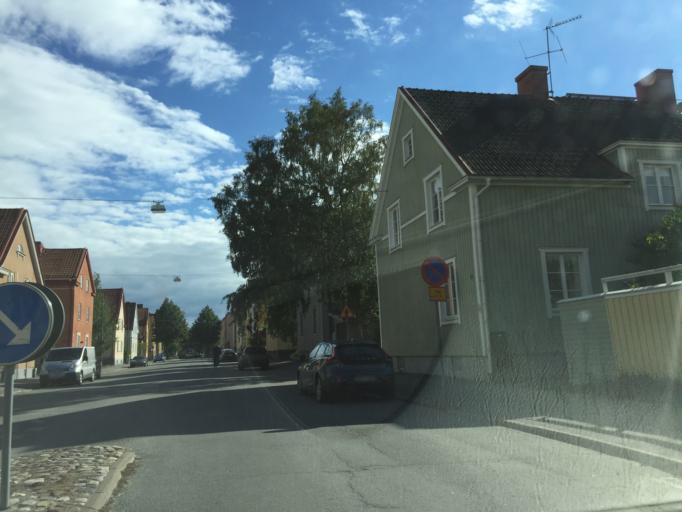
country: SE
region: OErebro
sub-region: Orebro Kommun
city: Orebro
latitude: 59.2851
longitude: 15.2273
